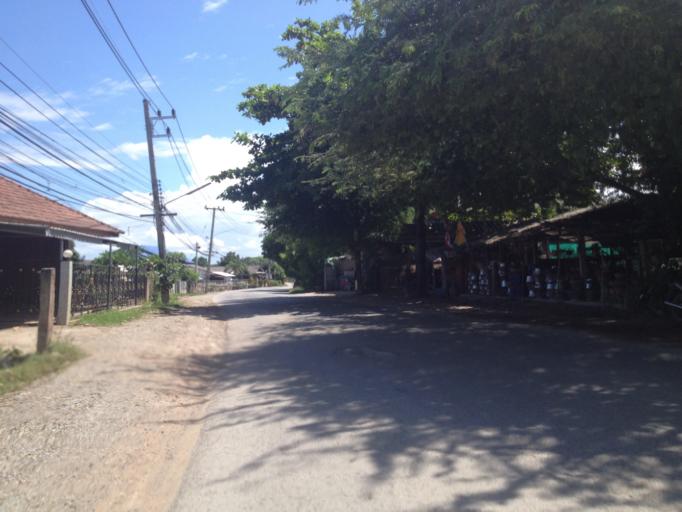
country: TH
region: Chiang Mai
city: San Pa Tong
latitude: 18.6431
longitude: 98.9280
